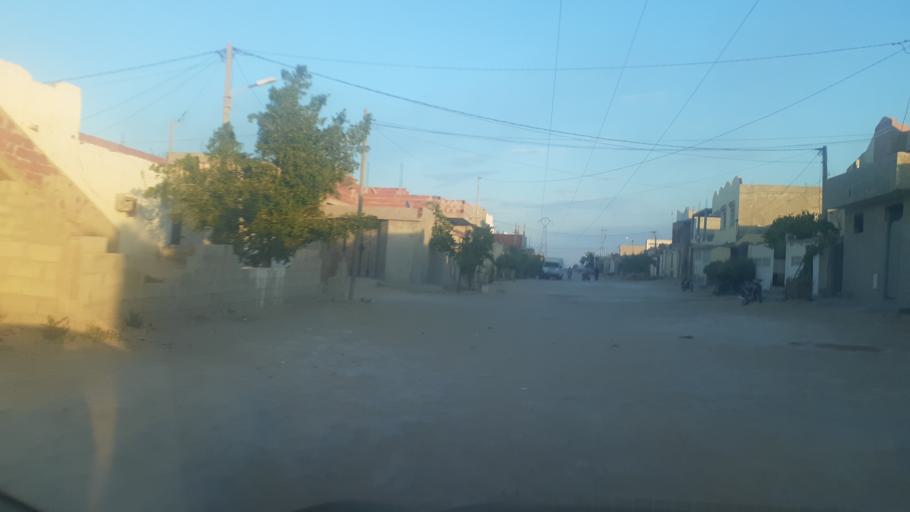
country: TN
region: Qabis
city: Gabes
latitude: 33.9332
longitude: 10.0386
